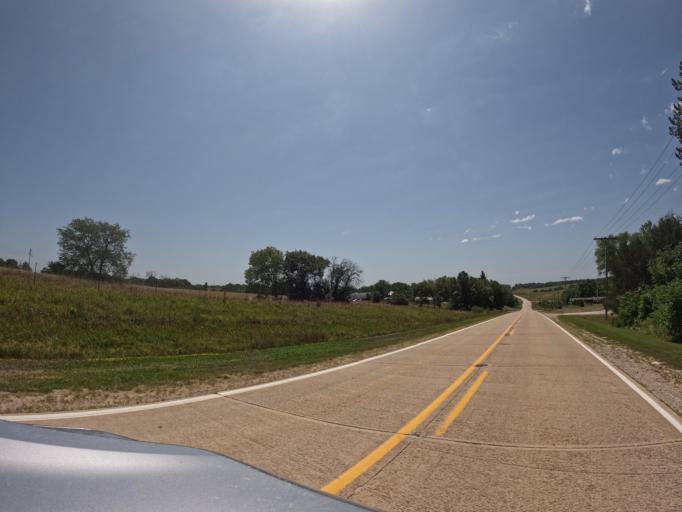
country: US
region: Iowa
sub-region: Henry County
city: Mount Pleasant
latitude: 40.9323
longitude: -91.5546
